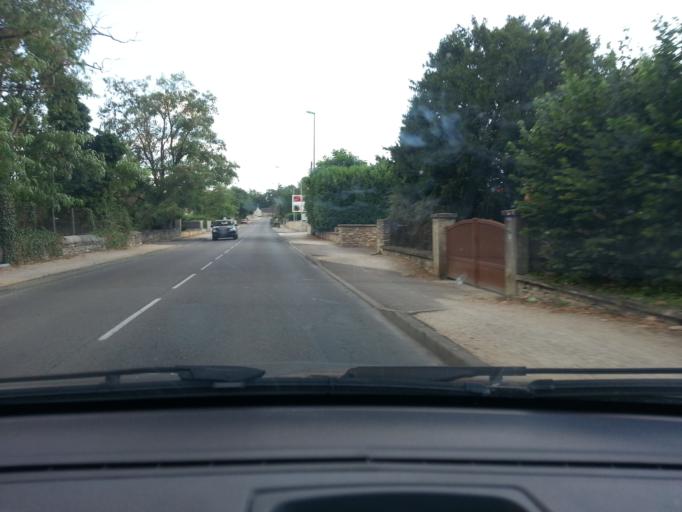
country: FR
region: Bourgogne
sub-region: Departement de Saone-et-Loire
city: Givry
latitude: 46.7773
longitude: 4.7392
